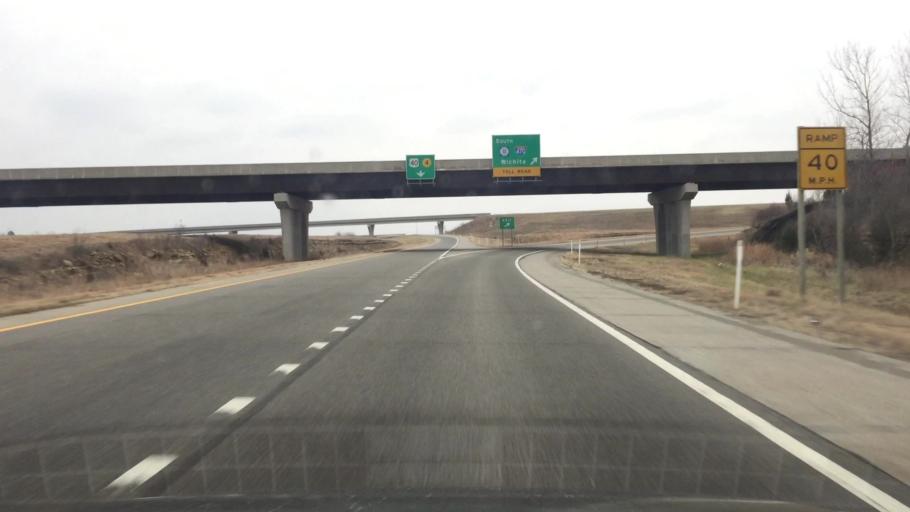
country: US
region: Kansas
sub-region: Shawnee County
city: Topeka
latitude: 39.0345
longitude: -95.6147
